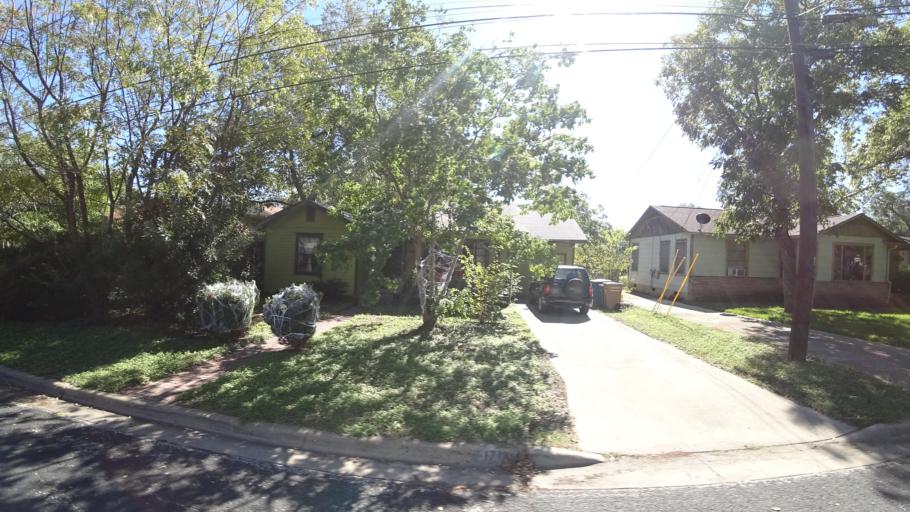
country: US
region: Texas
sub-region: Travis County
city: Austin
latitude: 30.2863
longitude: -97.7156
